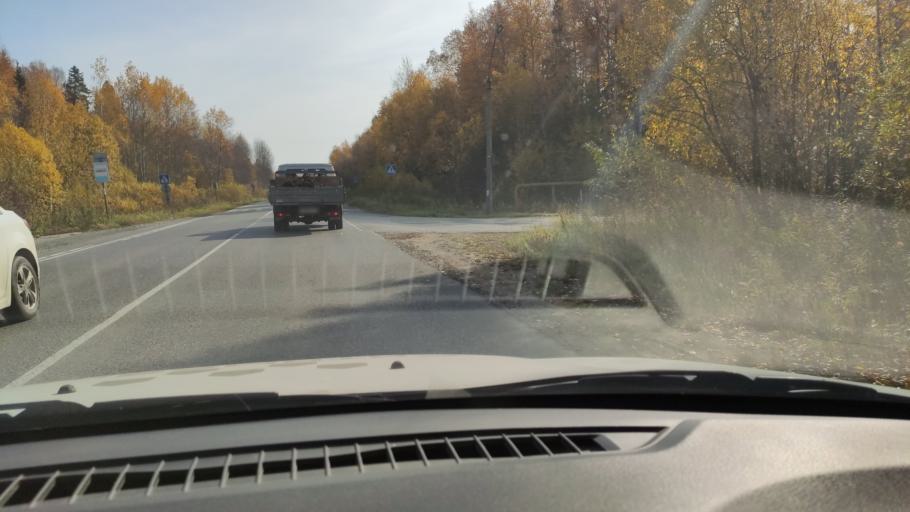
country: RU
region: Perm
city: Novyye Lyady
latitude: 58.0267
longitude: 56.6301
